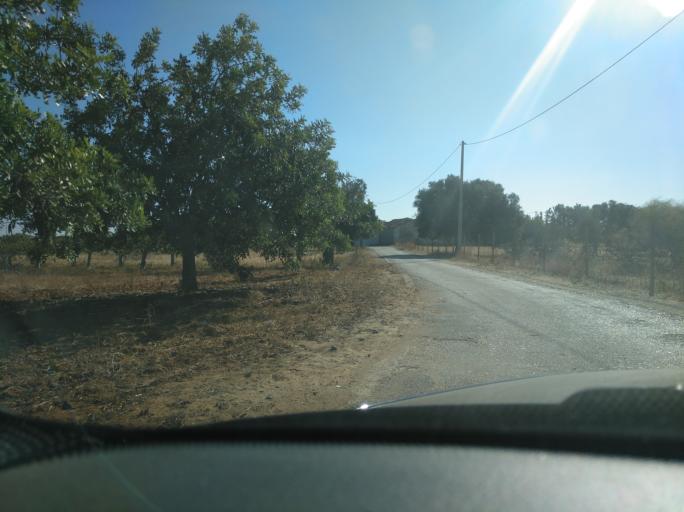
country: PT
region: Faro
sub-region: Vila Real de Santo Antonio
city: Monte Gordo
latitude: 37.1725
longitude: -7.5169
